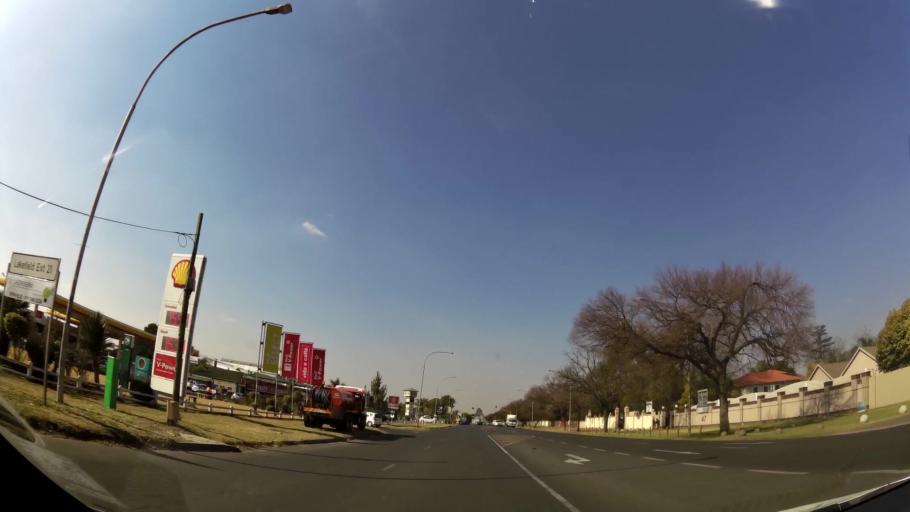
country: ZA
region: Gauteng
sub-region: Ekurhuleni Metropolitan Municipality
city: Benoni
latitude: -26.1790
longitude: 28.2850
